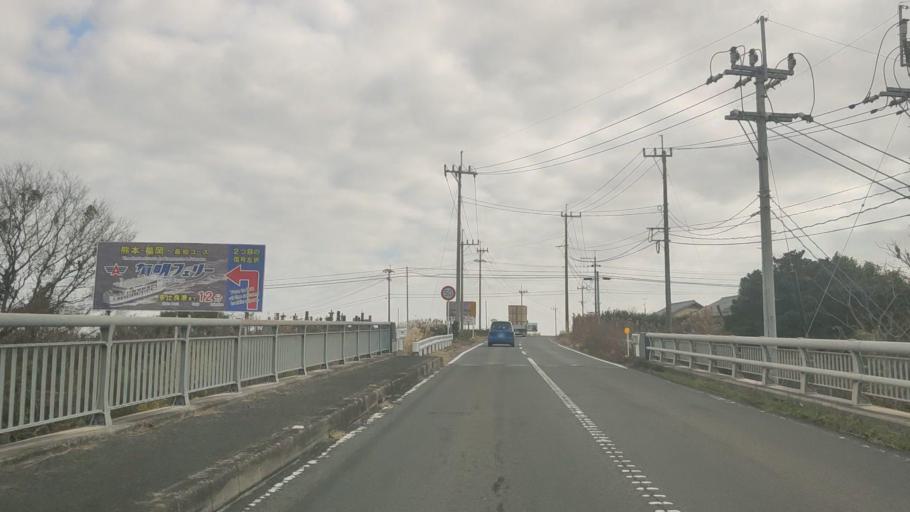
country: JP
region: Nagasaki
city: Shimabara
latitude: 32.8536
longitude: 130.2504
